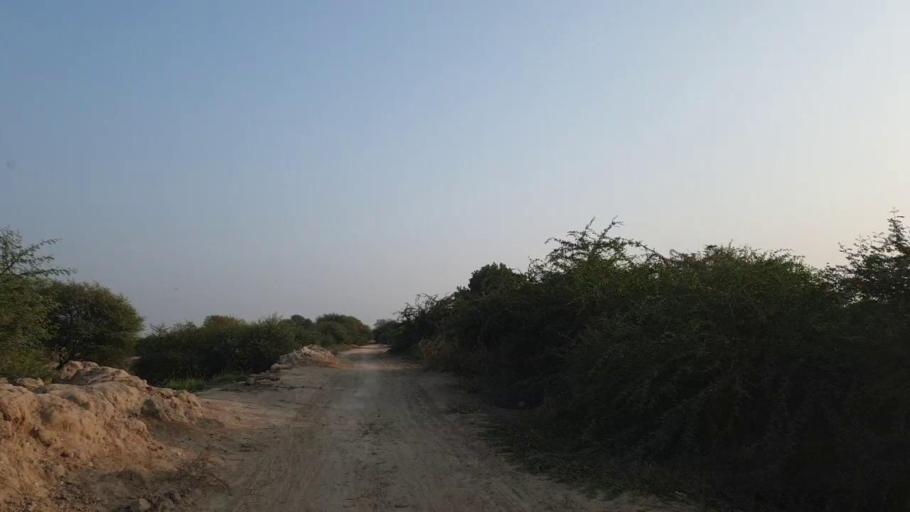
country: PK
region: Sindh
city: Kario
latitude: 24.8645
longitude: 68.6228
